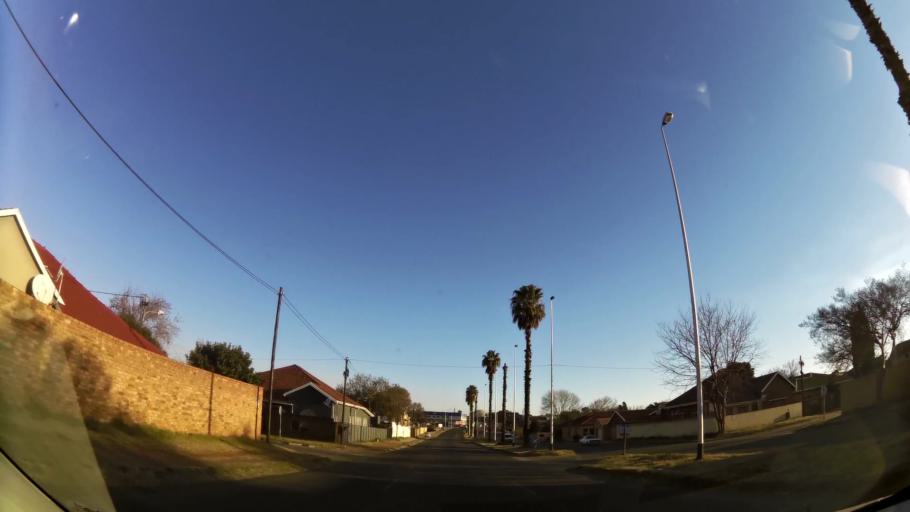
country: ZA
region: Gauteng
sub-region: City of Johannesburg Metropolitan Municipality
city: Roodepoort
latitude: -26.1610
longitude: 27.8735
